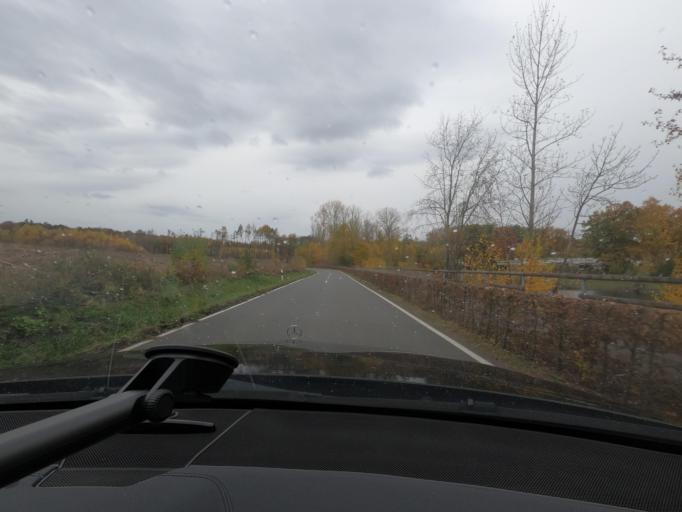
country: DE
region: North Rhine-Westphalia
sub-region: Regierungsbezirk Arnsberg
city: Mohnesee
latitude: 51.4776
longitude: 8.1062
